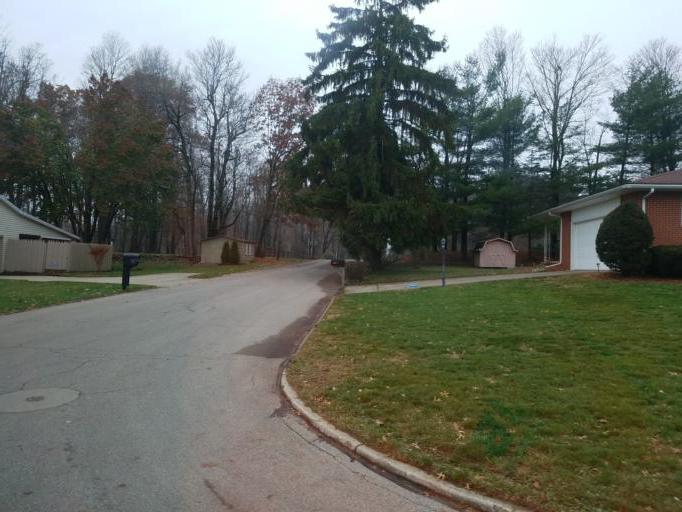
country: US
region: Ohio
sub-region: Richland County
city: Mansfield
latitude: 40.7195
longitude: -82.5308
